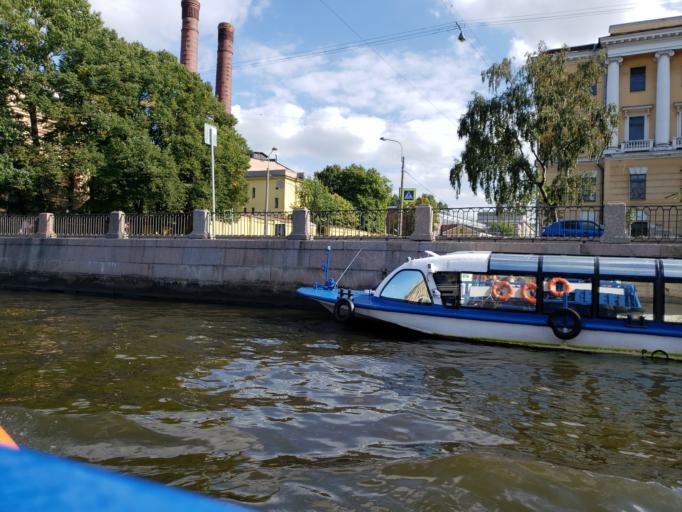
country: RU
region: St.-Petersburg
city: Saint Petersburg
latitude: 59.9230
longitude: 30.3217
